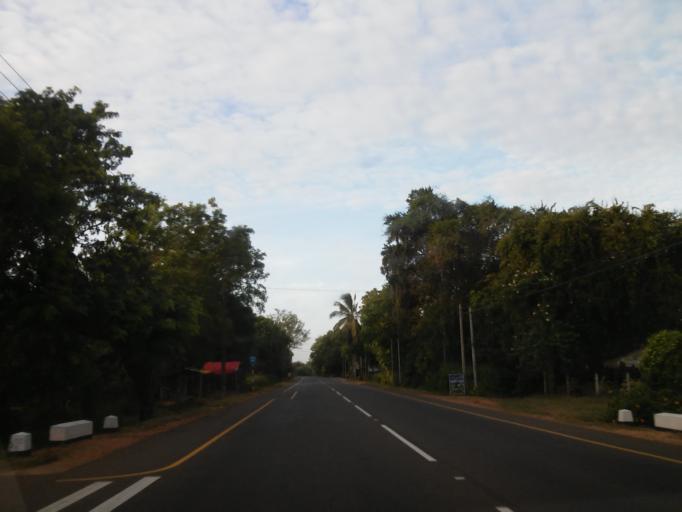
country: LK
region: North Central
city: Anuradhapura
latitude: 8.2328
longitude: 80.5228
